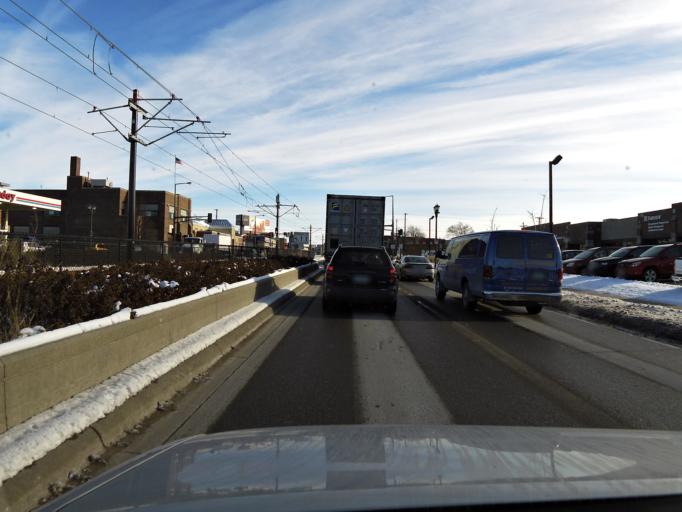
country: US
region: Minnesota
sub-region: Ramsey County
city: Falcon Heights
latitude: 44.9613
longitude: -93.1912
